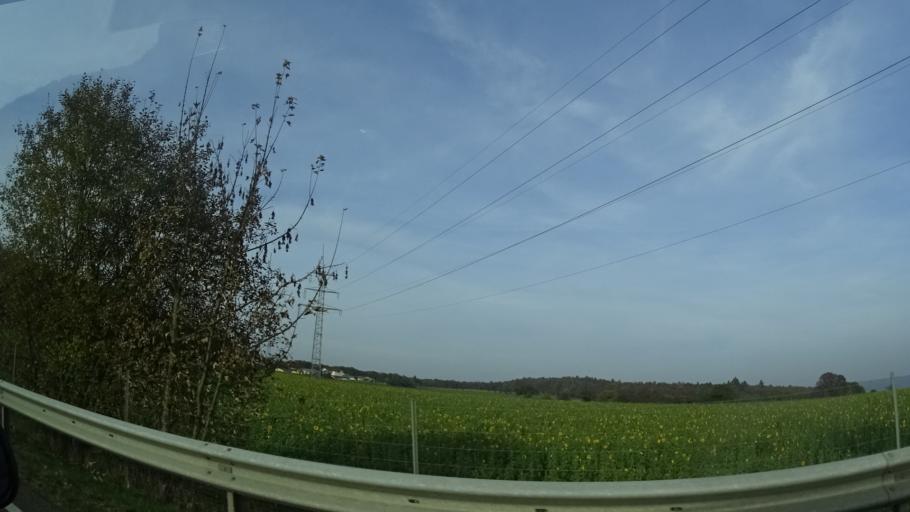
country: DE
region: Baden-Wuerttemberg
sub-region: Karlsruhe Region
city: Binau
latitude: 49.3563
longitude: 9.0367
